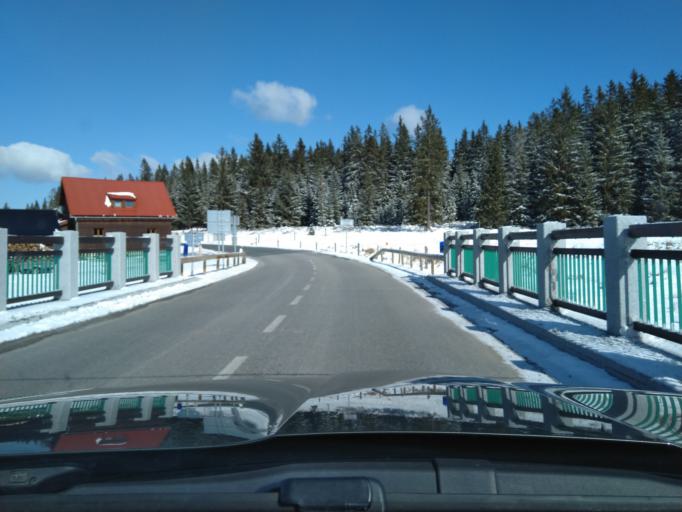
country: CZ
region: Plzensky
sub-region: Okres Klatovy
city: Kasperske Hory
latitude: 49.0483
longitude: 13.5775
